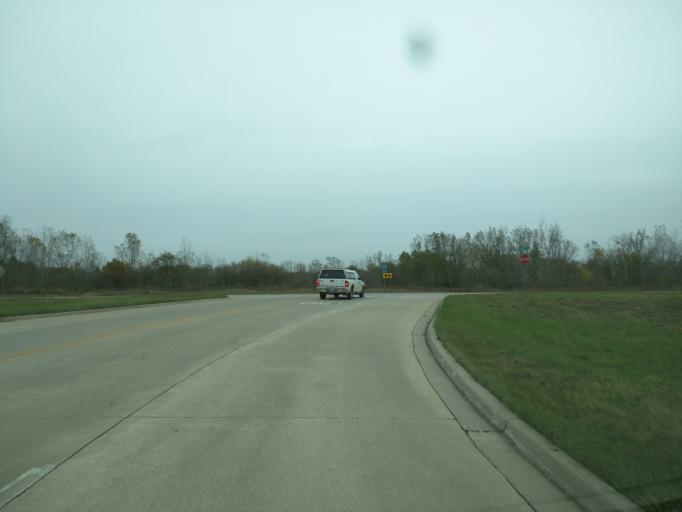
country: US
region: Michigan
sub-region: Ingham County
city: Edgemont Park
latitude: 42.7730
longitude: -84.5663
